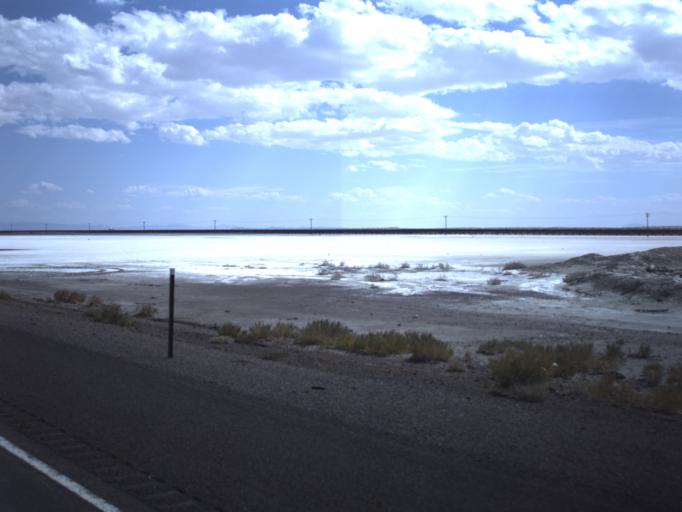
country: US
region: Utah
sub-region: Tooele County
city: Wendover
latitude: 40.7372
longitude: -113.7892
